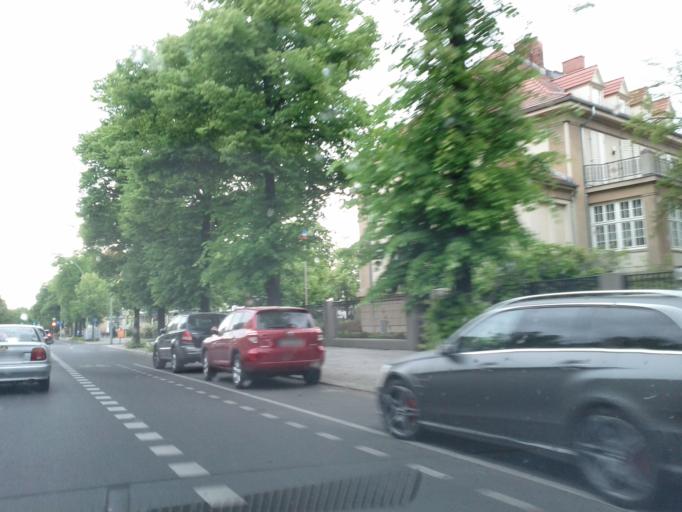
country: DE
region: Berlin
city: Westend
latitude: 52.5141
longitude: 13.2648
